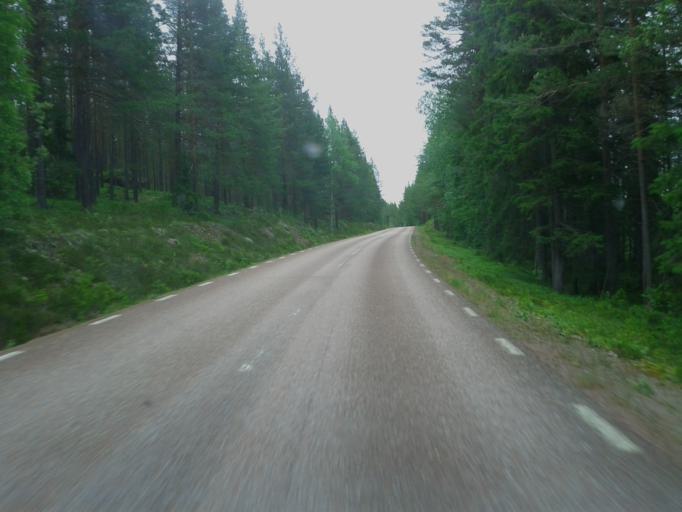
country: NO
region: Hedmark
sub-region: Trysil
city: Innbygda
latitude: 61.8353
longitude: 12.8264
